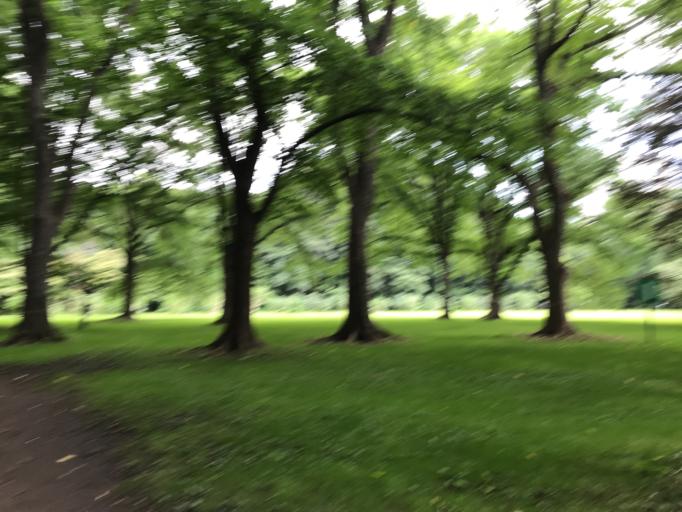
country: JP
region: Hokkaido
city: Sapporo
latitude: 43.0648
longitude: 141.3421
